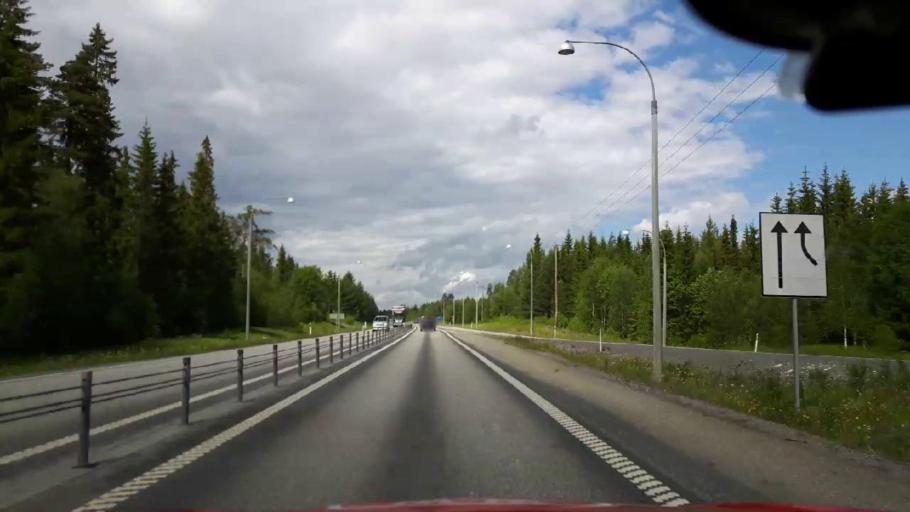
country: SE
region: Jaemtland
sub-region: OEstersunds Kommun
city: Ostersund
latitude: 63.2199
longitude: 14.6291
